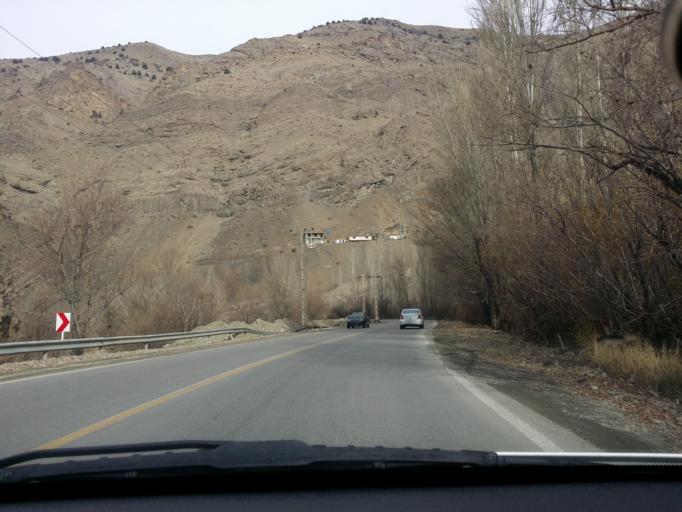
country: IR
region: Tehran
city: Tajrish
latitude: 36.0170
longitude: 51.2791
